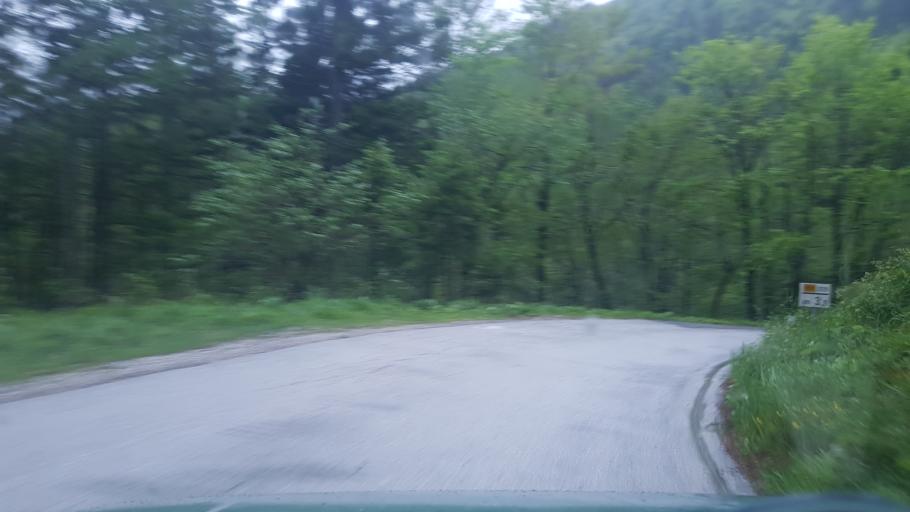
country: SI
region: Bohinj
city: Bohinjska Bistrica
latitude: 46.2153
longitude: 14.0082
